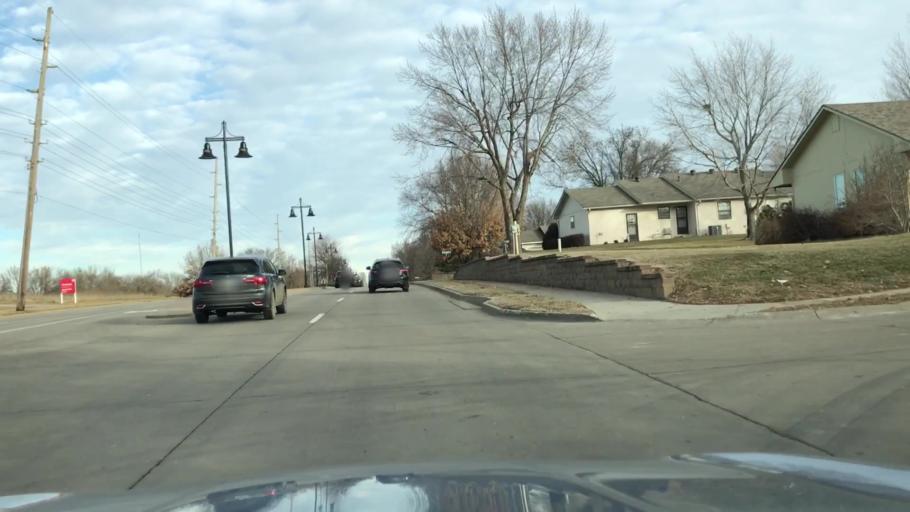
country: US
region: Missouri
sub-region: Jackson County
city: Lees Summit
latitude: 38.9168
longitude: -94.4132
